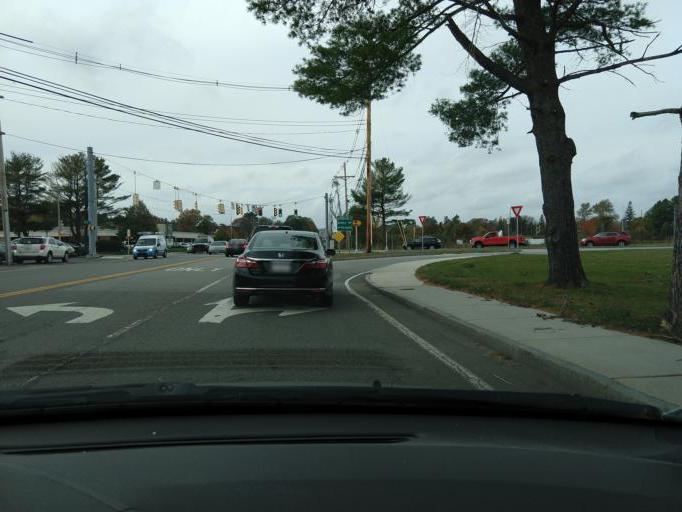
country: US
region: Massachusetts
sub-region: Middlesex County
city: Pinehurst
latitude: 42.5018
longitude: -71.2332
